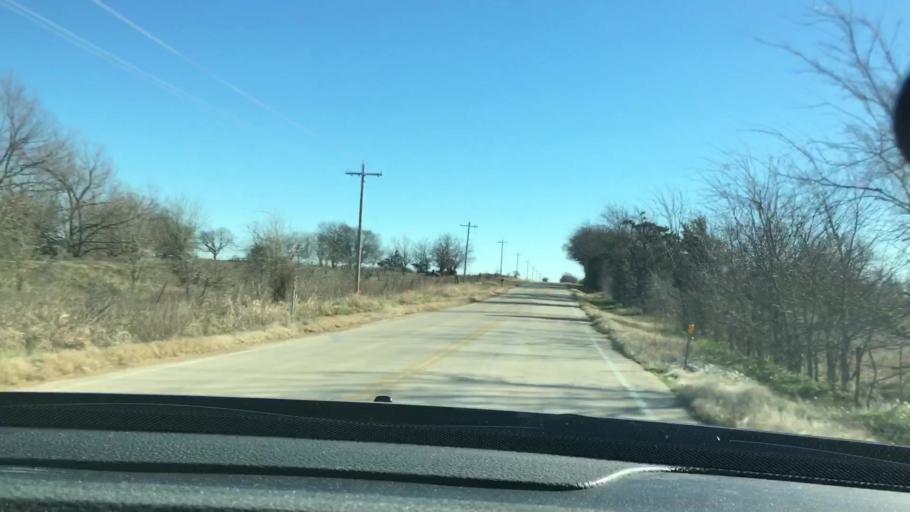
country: US
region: Oklahoma
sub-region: Marshall County
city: Madill
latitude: 34.1144
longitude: -96.6695
